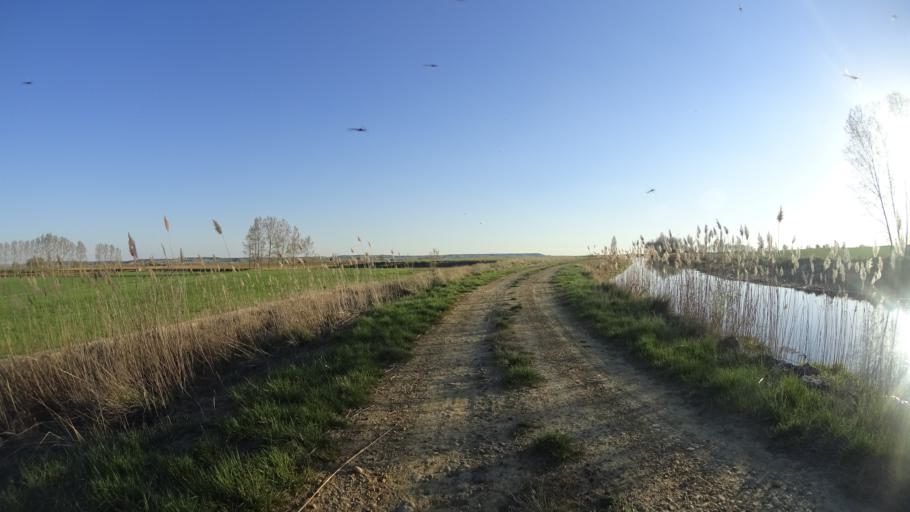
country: ES
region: Castille and Leon
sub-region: Provincia de Palencia
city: Boadilla del Camino
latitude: 42.2615
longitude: -4.3596
